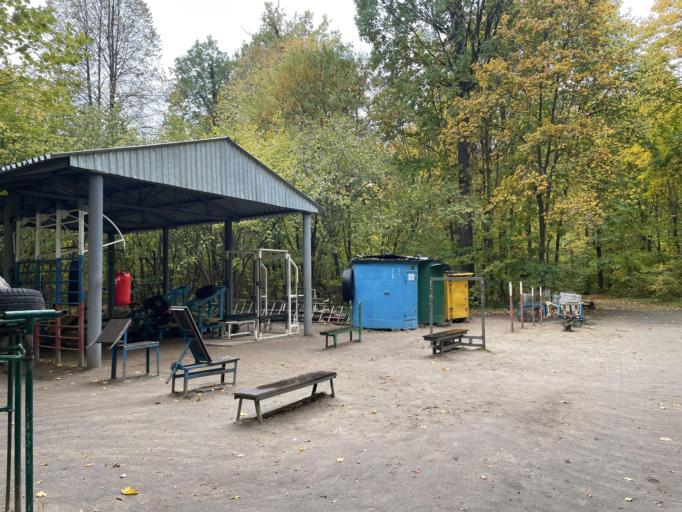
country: RU
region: Chuvashia
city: Novocheboksarsk
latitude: 56.1201
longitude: 47.4669
